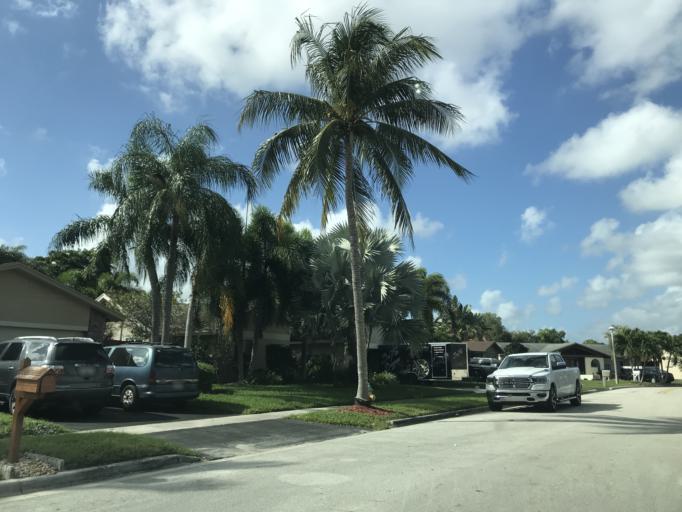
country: US
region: Florida
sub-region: Broward County
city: Coconut Creek
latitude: 26.2664
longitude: -80.1967
